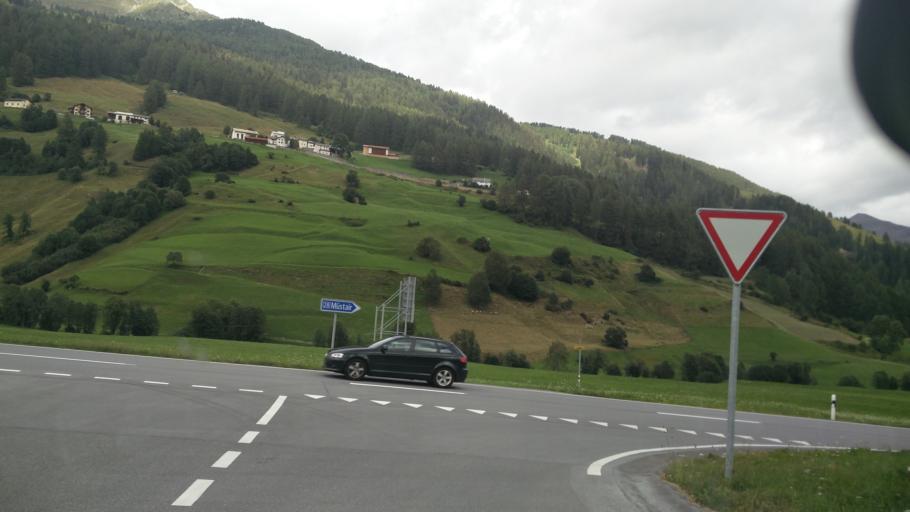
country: IT
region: Trentino-Alto Adige
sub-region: Bolzano
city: Tubre
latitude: 46.6077
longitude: 10.3740
